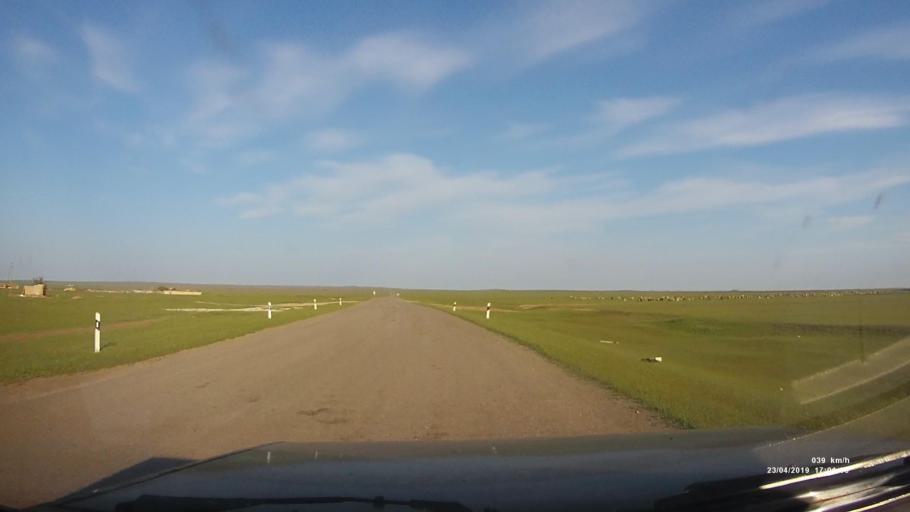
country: RU
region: Kalmykiya
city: Priyutnoye
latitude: 46.2947
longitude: 43.4088
